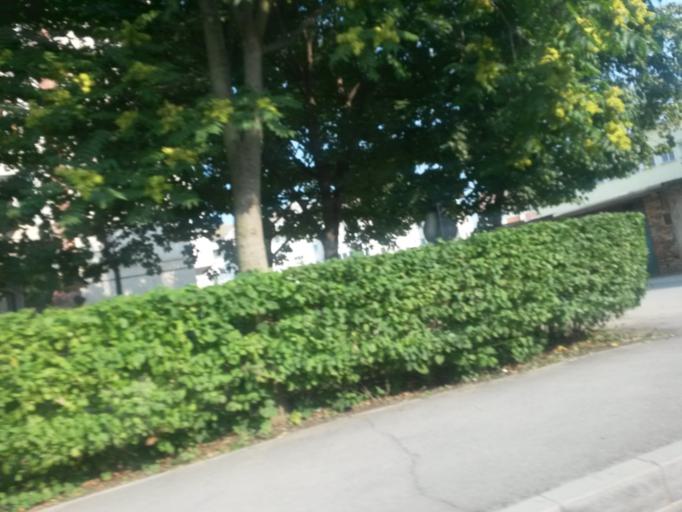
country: RO
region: Cluj
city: Turda
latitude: 46.5667
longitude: 23.7799
